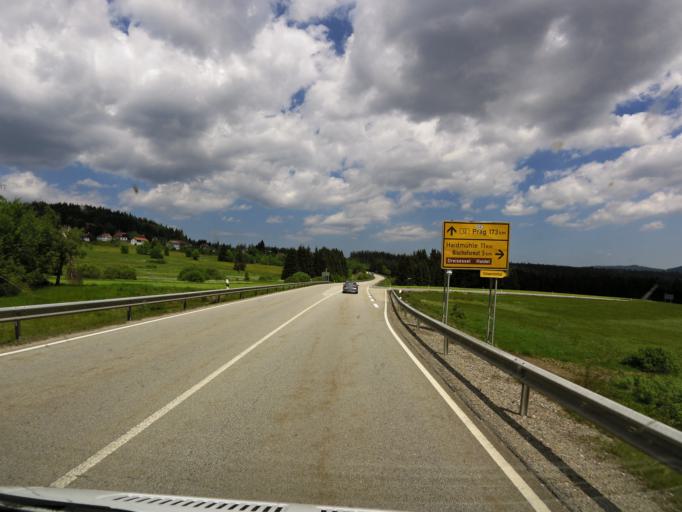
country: DE
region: Bavaria
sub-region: Lower Bavaria
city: Philippsreut
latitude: 48.8633
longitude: 13.6799
